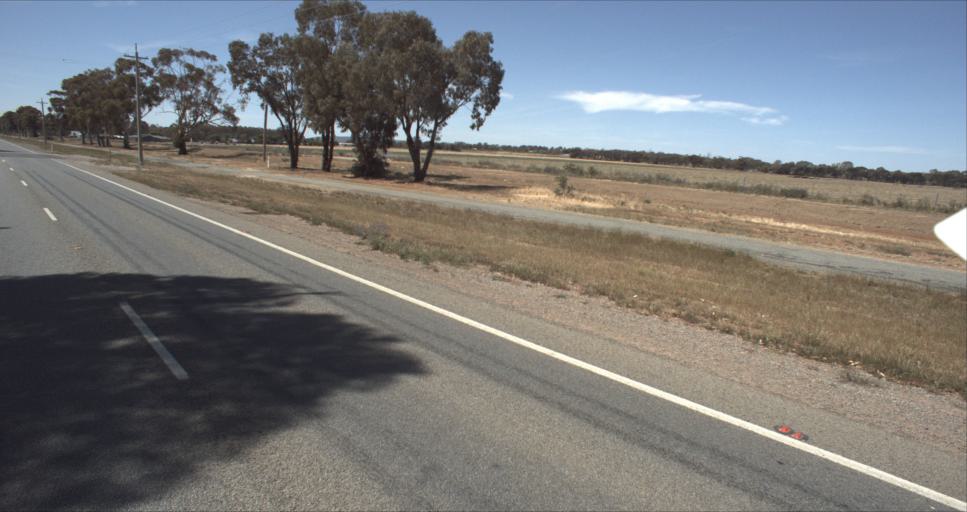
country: AU
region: New South Wales
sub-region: Leeton
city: Leeton
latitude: -34.5903
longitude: 146.4138
